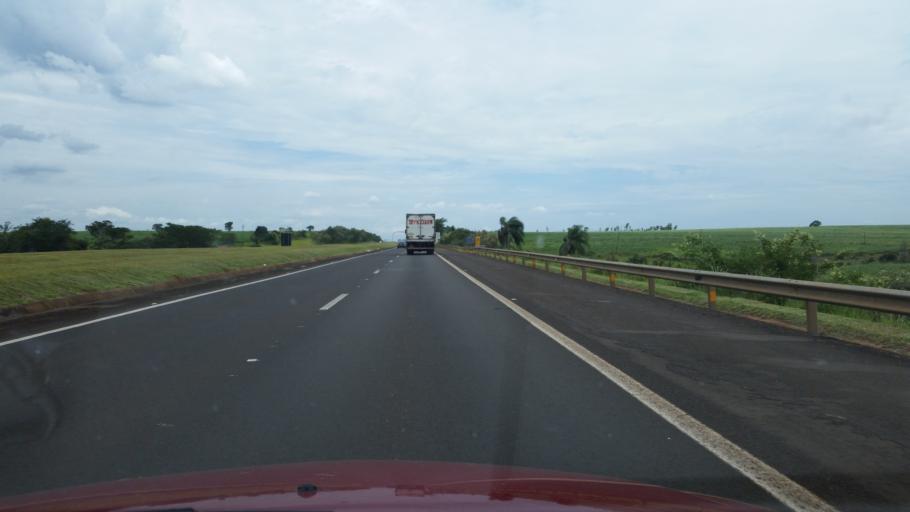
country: BR
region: Sao Paulo
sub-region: Avare
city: Avare
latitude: -22.9692
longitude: -48.7980
